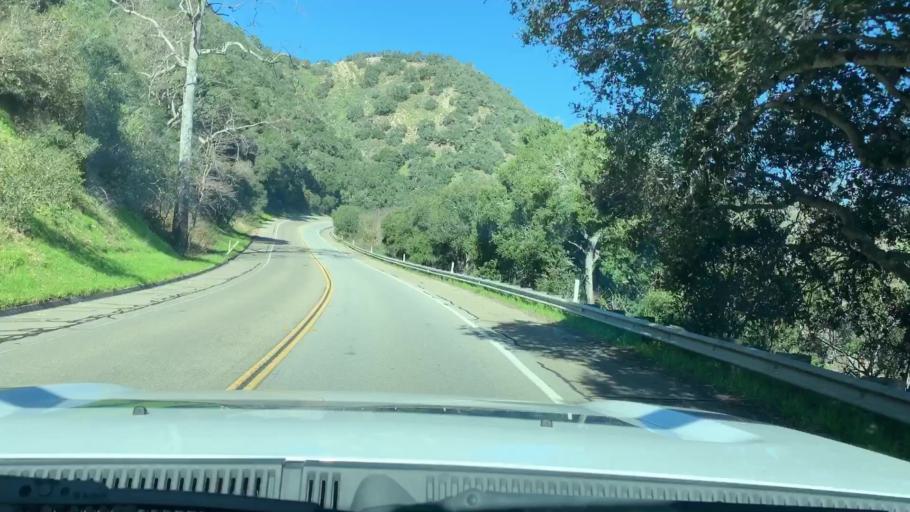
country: US
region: California
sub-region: San Luis Obispo County
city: Pismo Beach
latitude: 35.1604
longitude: -120.6328
